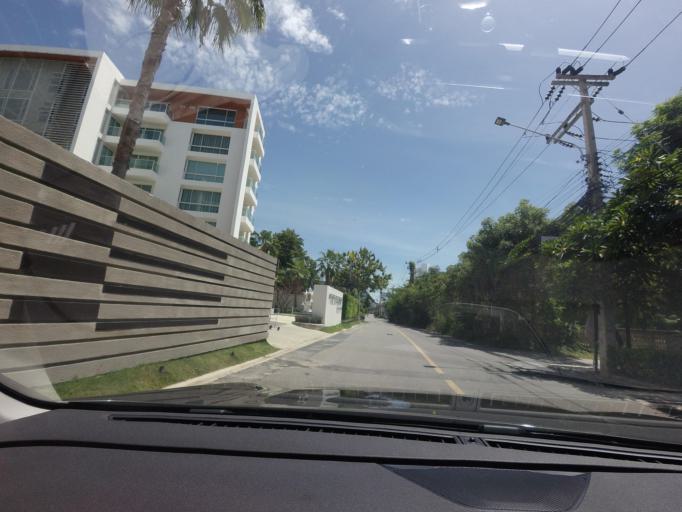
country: TH
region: Prachuap Khiri Khan
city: Hua Hin
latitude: 12.5114
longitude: 99.9757
